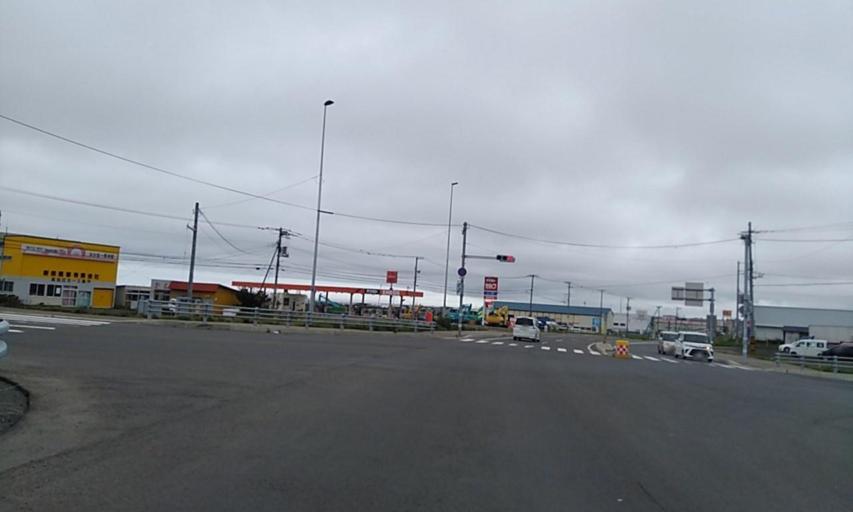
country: JP
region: Hokkaido
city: Nemuro
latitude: 43.3155
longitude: 145.5510
